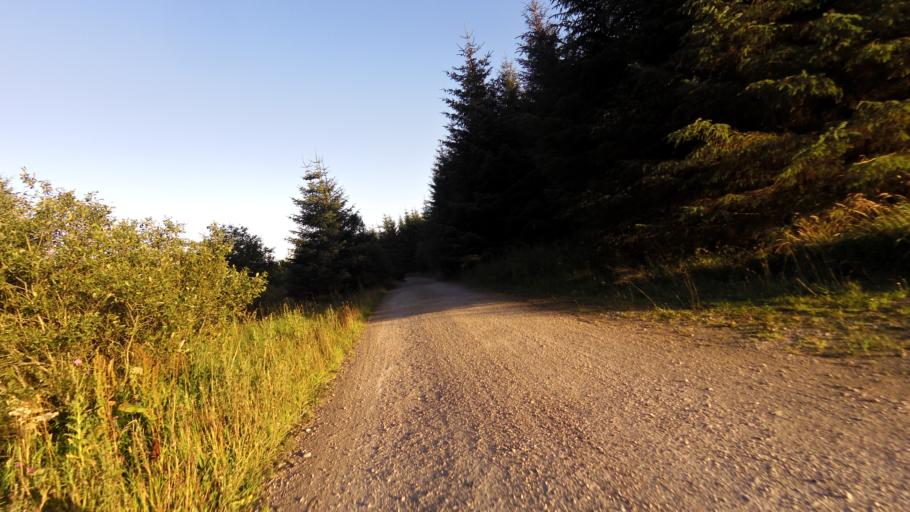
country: GB
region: England
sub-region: North Yorkshire
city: Settle
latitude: 54.0096
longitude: -2.3780
